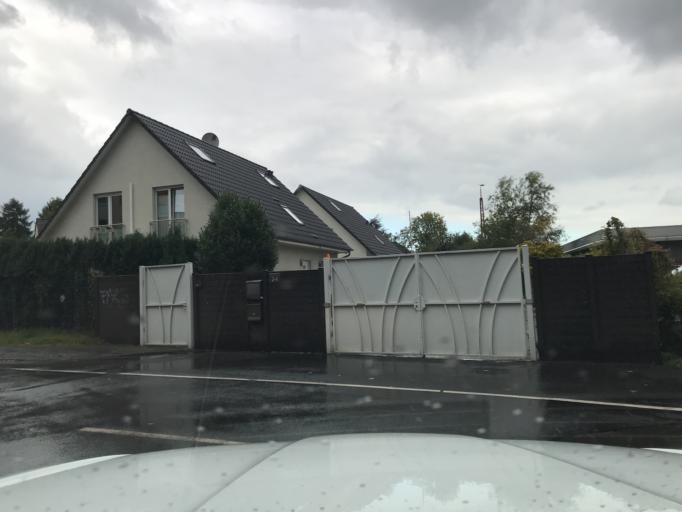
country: DE
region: North Rhine-Westphalia
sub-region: Regierungsbezirk Dusseldorf
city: Muelheim (Ruhr)
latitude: 51.4243
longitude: 6.8449
